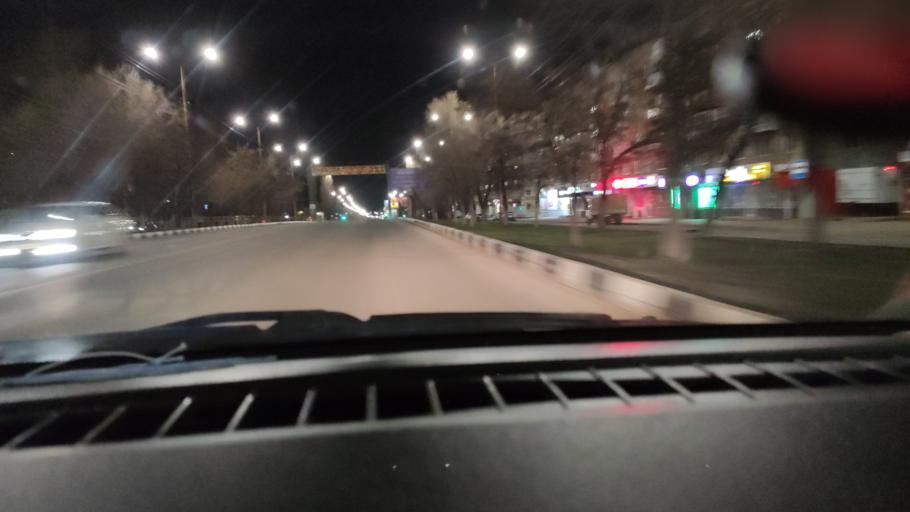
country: RU
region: Saratov
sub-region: Saratovskiy Rayon
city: Saratov
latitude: 51.6011
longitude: 45.9687
